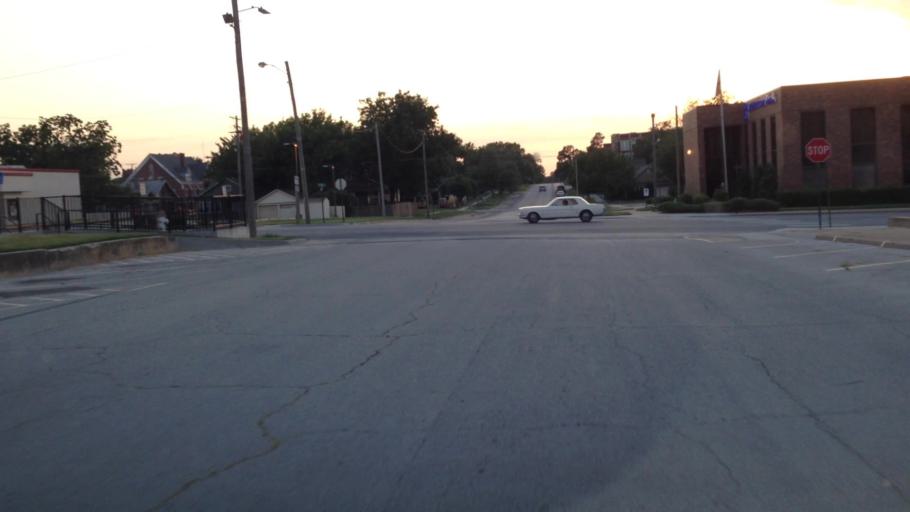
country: US
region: Kansas
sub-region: Montgomery County
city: Independence
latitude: 37.2277
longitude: -95.7061
